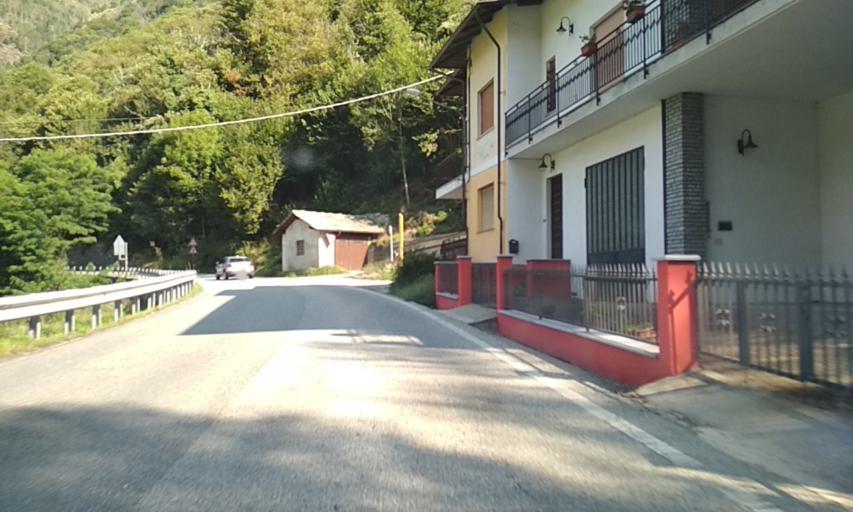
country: IT
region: Piedmont
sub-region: Provincia di Torino
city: Locana
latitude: 45.4104
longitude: 7.4816
